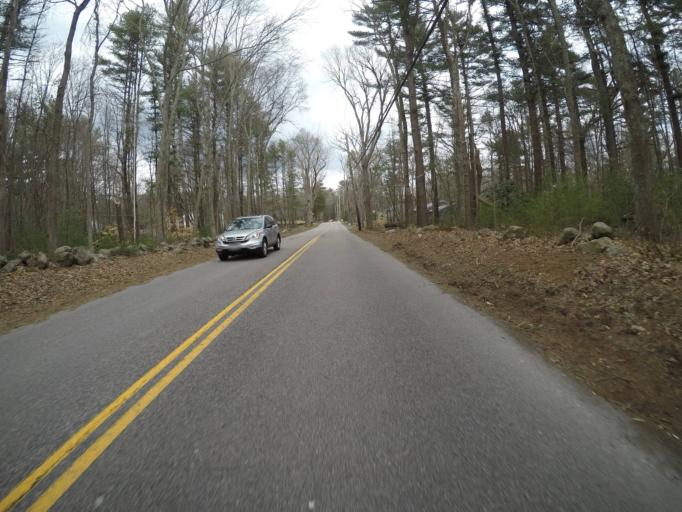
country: US
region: Massachusetts
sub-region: Bristol County
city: Easton
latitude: 42.0475
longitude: -71.1154
